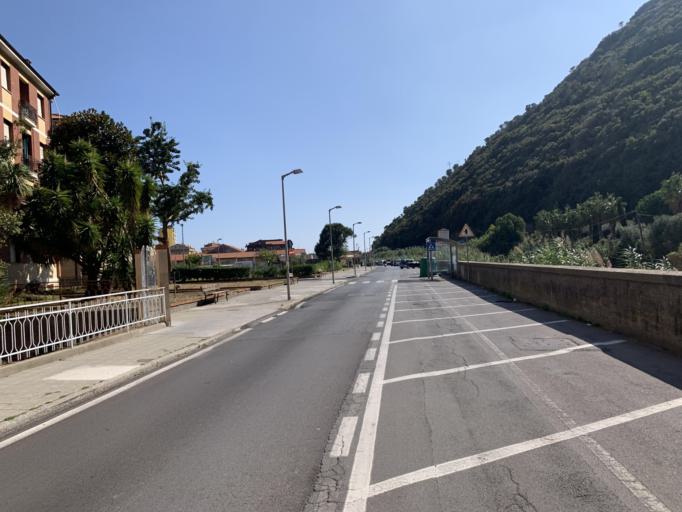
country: IT
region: Liguria
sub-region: Provincia di Savona
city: Finale Ligure
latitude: 44.1727
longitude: 8.3316
